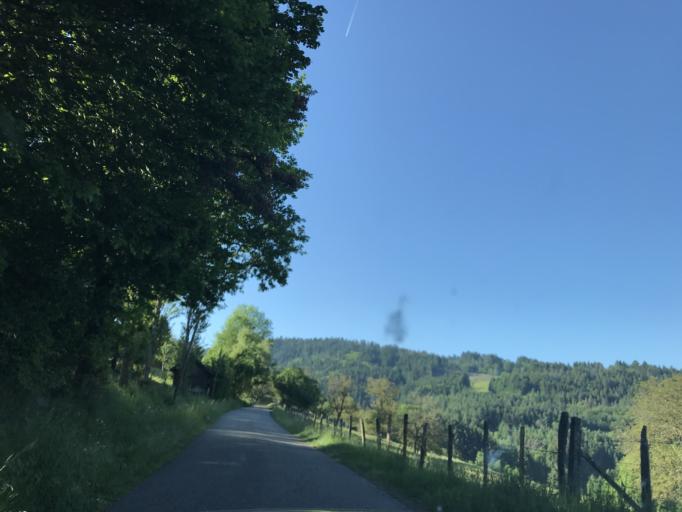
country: FR
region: Auvergne
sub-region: Departement du Puy-de-Dome
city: Job
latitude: 45.6397
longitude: 3.6678
